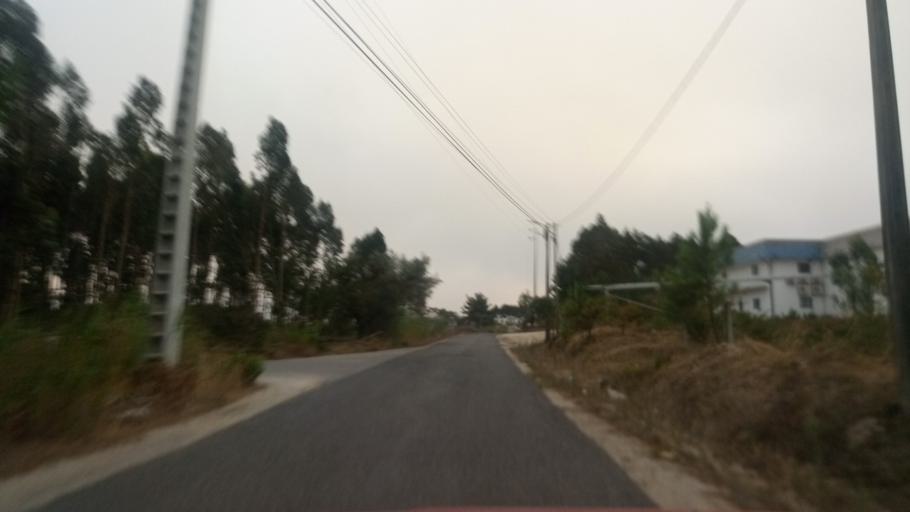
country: PT
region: Leiria
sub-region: Caldas da Rainha
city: Caldas da Rainha
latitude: 39.4257
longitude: -9.1524
